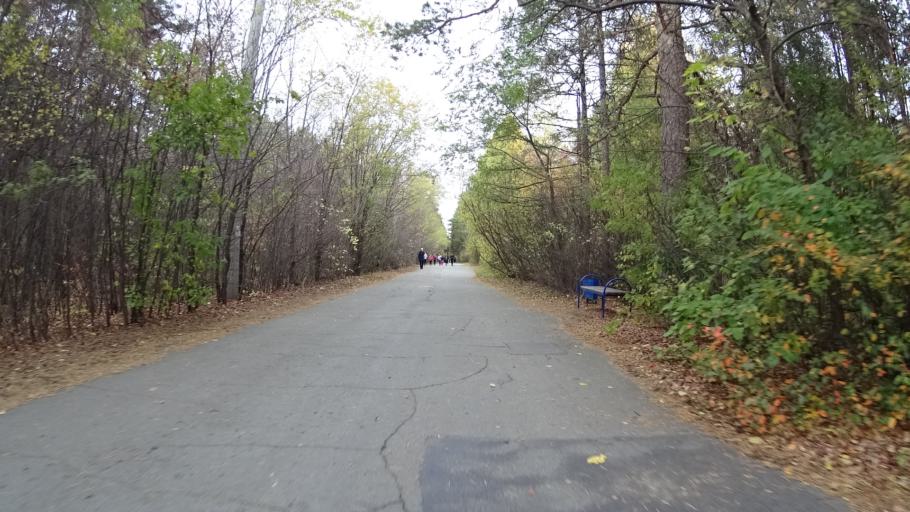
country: RU
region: Chelyabinsk
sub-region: Gorod Chelyabinsk
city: Chelyabinsk
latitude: 55.1504
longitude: 61.3567
